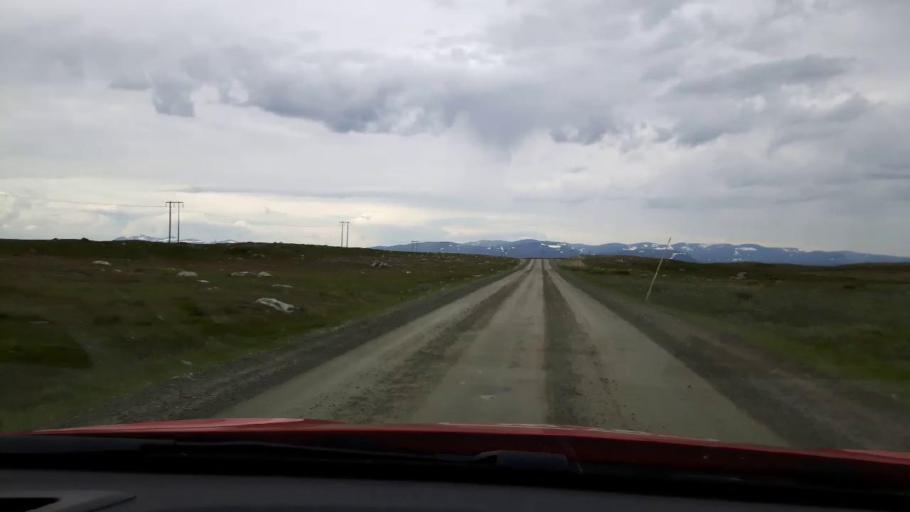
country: SE
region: Jaemtland
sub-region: Are Kommun
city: Are
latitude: 62.7486
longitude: 12.7479
